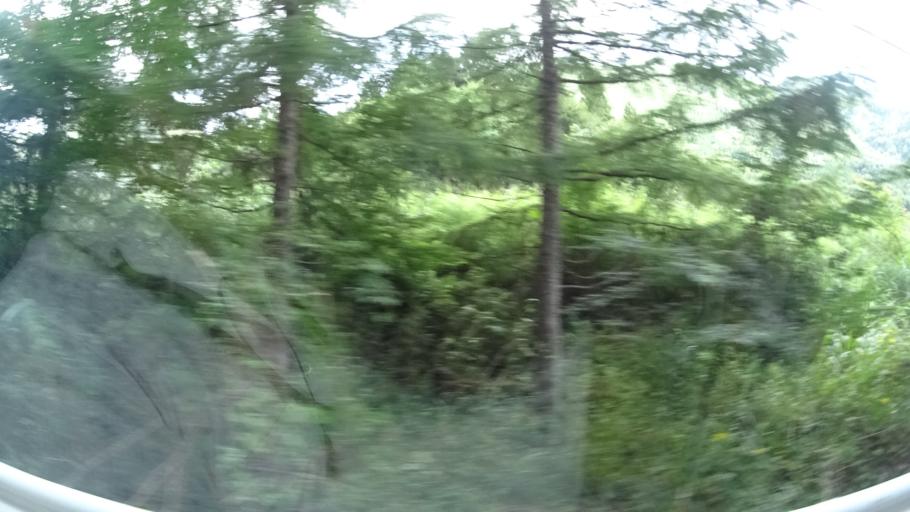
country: JP
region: Tochigi
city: Nikko
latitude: 36.6747
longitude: 139.4826
